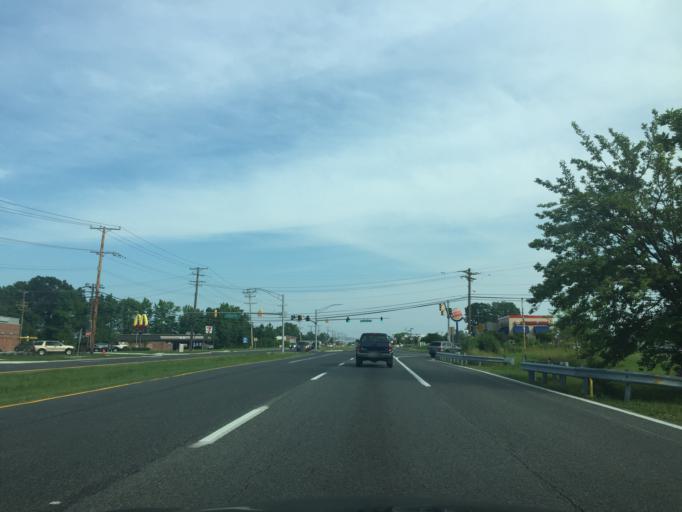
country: US
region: Maryland
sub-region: Baltimore County
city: Essex
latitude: 39.2725
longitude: -76.4722
